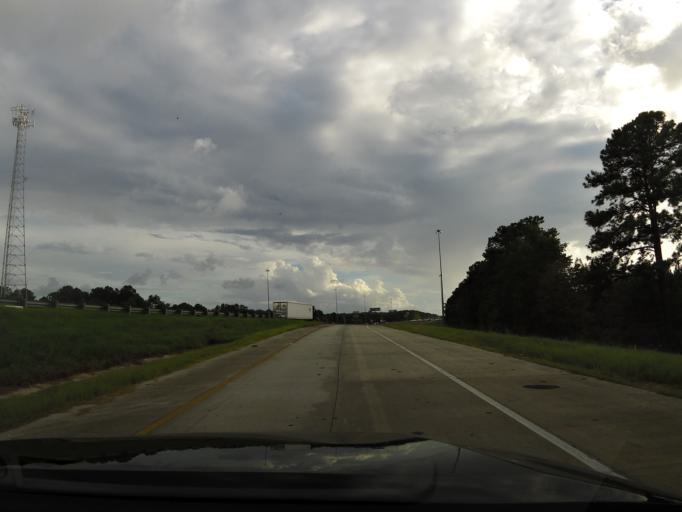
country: US
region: Georgia
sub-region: Liberty County
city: Midway
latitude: 31.6533
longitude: -81.3958
